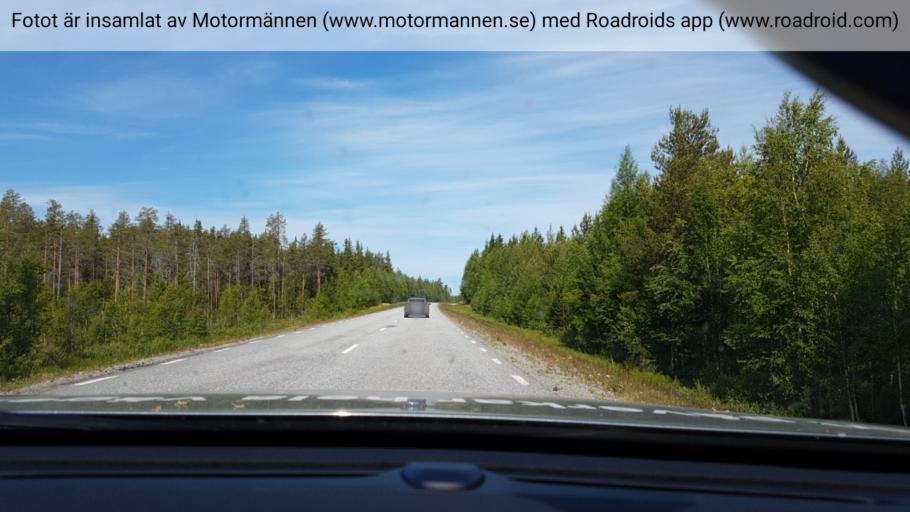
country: SE
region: Vaesterbotten
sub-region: Asele Kommun
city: Asele
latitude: 64.2097
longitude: 16.9285
